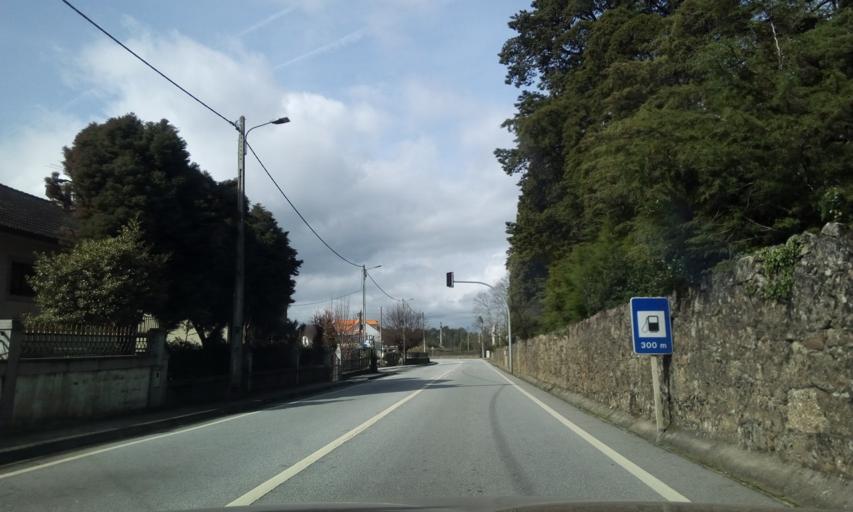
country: PT
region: Viseu
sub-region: Satao
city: Satao
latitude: 40.6704
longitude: -7.7048
